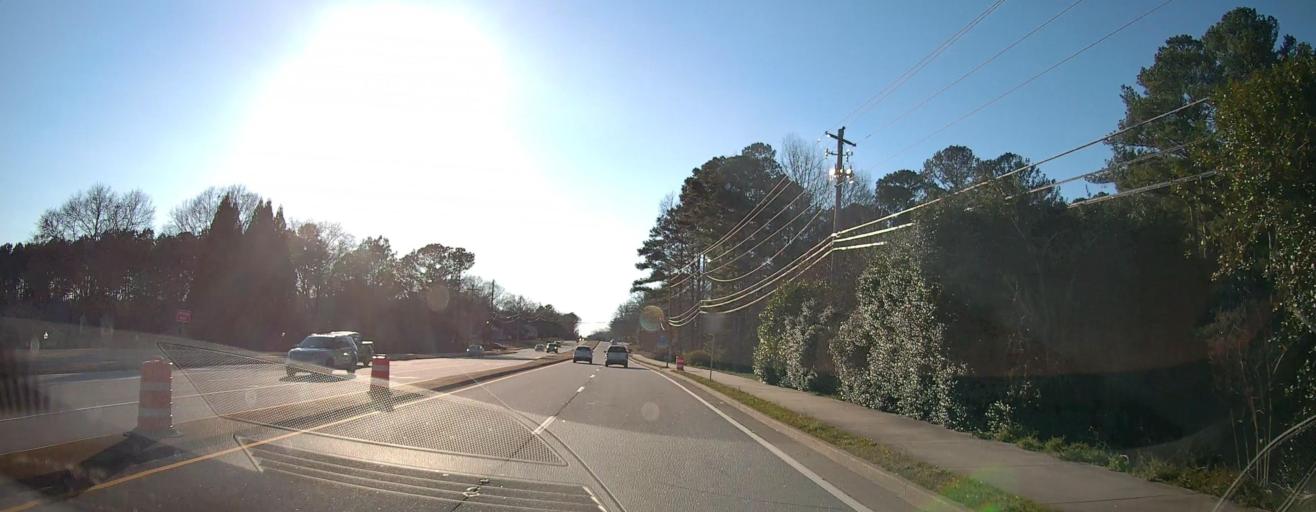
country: US
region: Georgia
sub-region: Fayette County
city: Fayetteville
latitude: 33.4509
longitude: -84.4386
